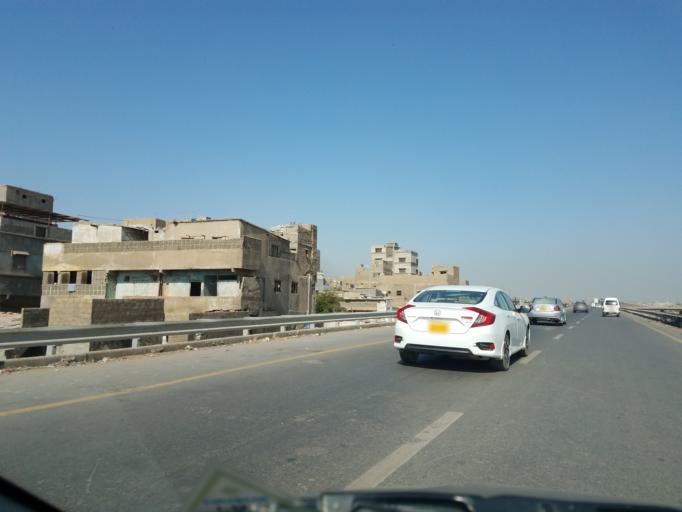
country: PK
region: Sindh
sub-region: Karachi District
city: Karachi
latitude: 24.8793
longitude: 66.9893
